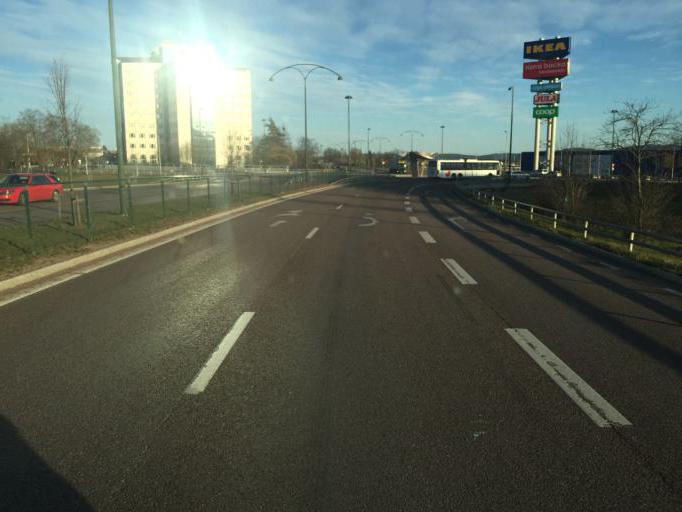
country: SE
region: Dalarna
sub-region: Borlange Kommun
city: Borlaenge
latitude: 60.4846
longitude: 15.4207
